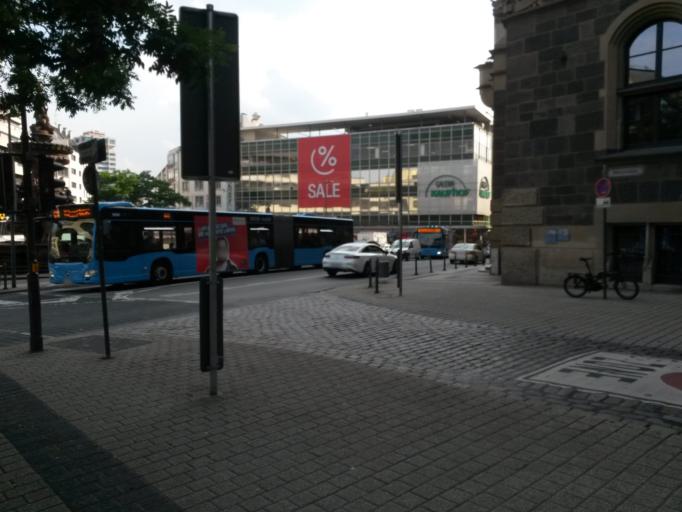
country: DE
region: North Rhine-Westphalia
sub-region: Regierungsbezirk Dusseldorf
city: Wuppertal
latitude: 51.2591
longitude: 7.1467
